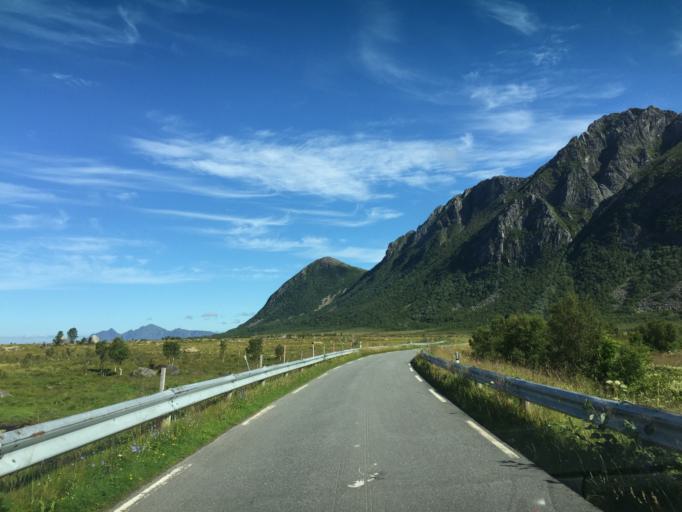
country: NO
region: Nordland
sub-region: Vagan
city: Svolvaer
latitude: 68.3978
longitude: 14.5660
